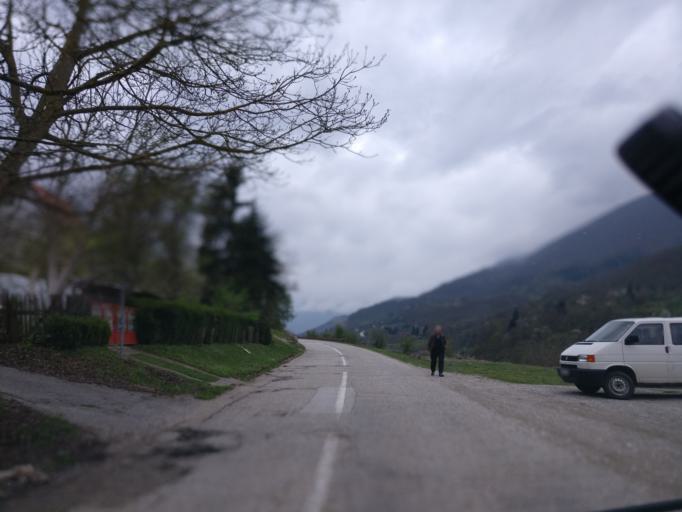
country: BA
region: Republika Srpska
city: Foca
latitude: 43.4470
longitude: 18.7558
